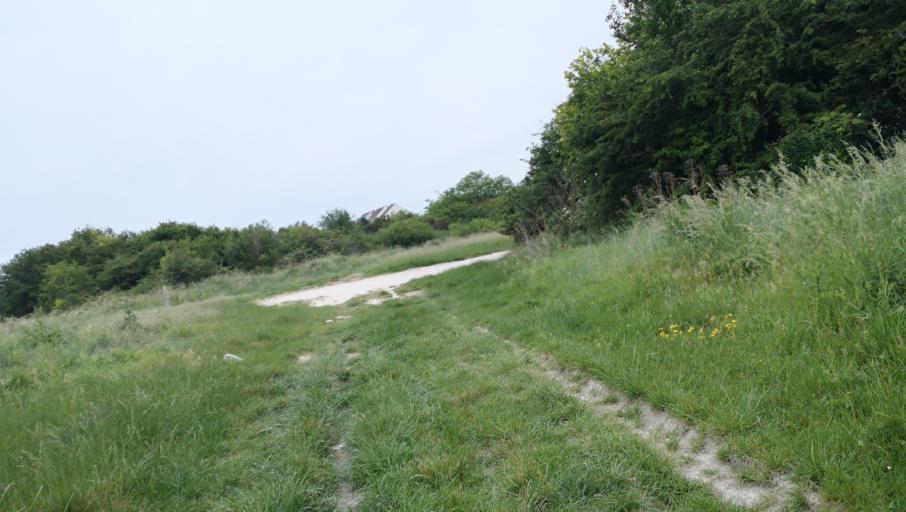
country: FR
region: Centre
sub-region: Departement du Loiret
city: Orleans
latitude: 47.9160
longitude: 1.8904
